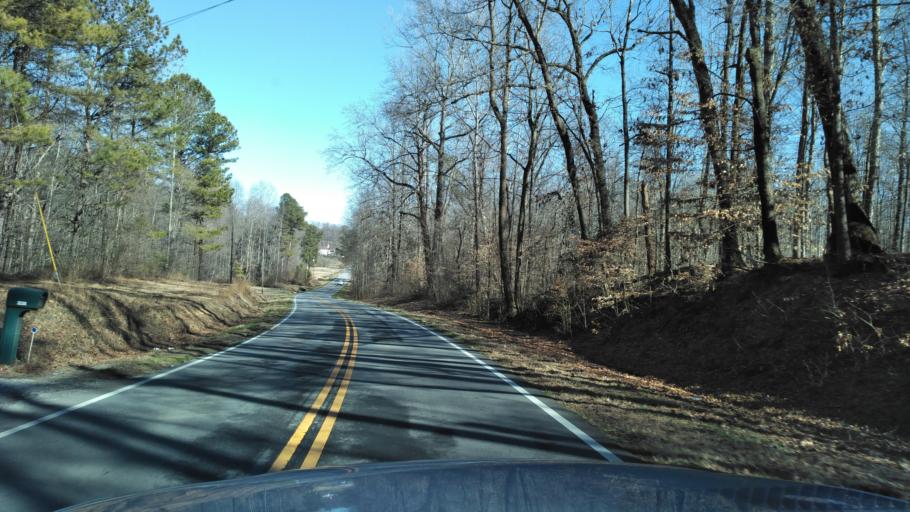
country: US
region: Georgia
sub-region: Hall County
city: Gainesville
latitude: 34.3090
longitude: -83.7383
